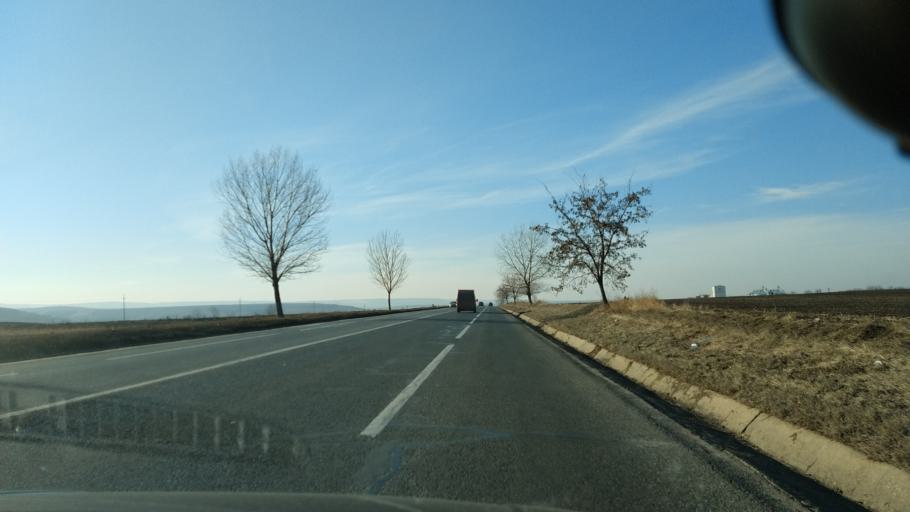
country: RO
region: Iasi
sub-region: Comuna Ion Neculce
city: Razboieni
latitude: 47.2211
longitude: 27.0782
